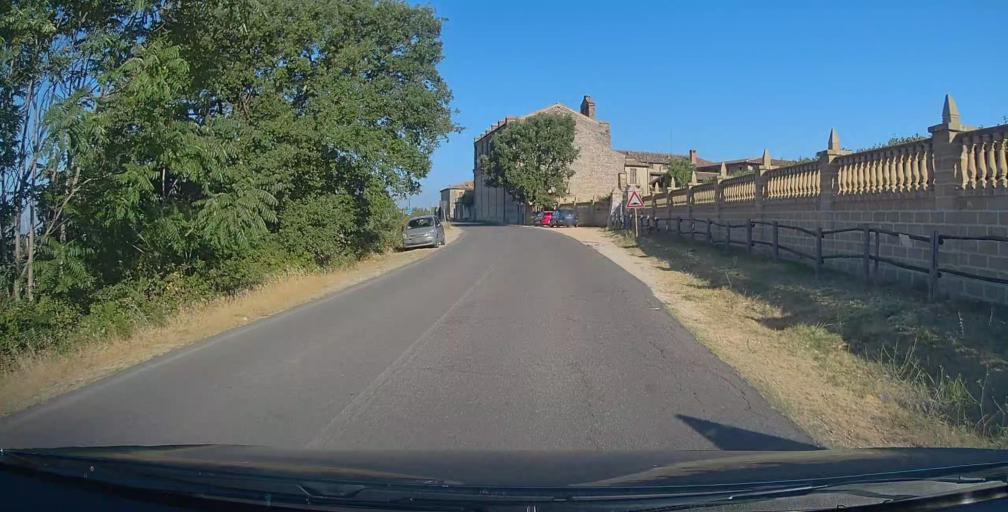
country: IT
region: Umbria
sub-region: Provincia di Terni
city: Calvi dell'Umbria
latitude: 42.4073
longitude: 12.5643
